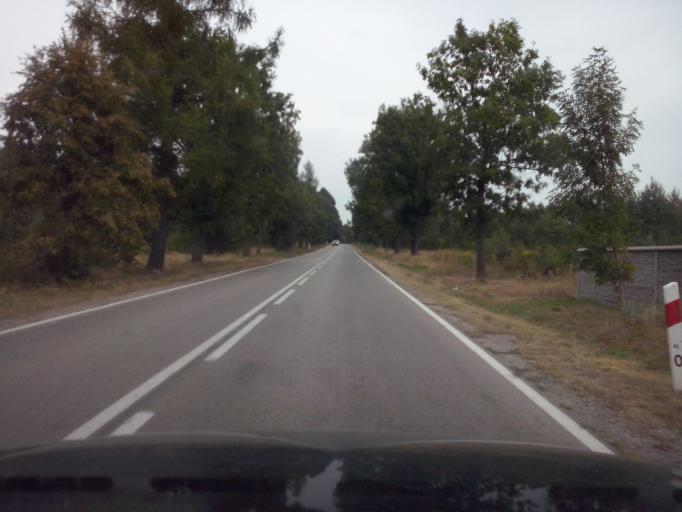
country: PL
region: Swietokrzyskie
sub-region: Powiat kielecki
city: Rakow
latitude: 50.6838
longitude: 21.0546
